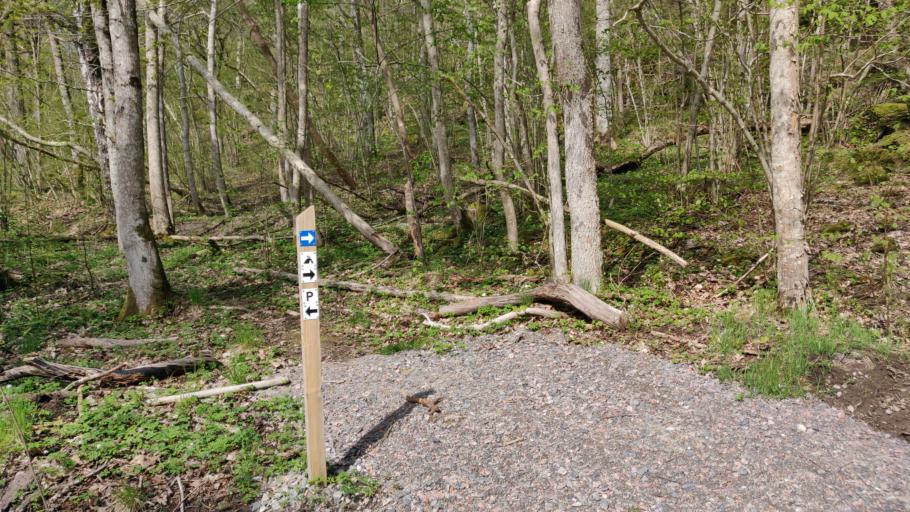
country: SE
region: Vaestra Goetaland
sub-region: Munkedals Kommun
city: Munkedal
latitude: 58.4631
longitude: 11.6922
